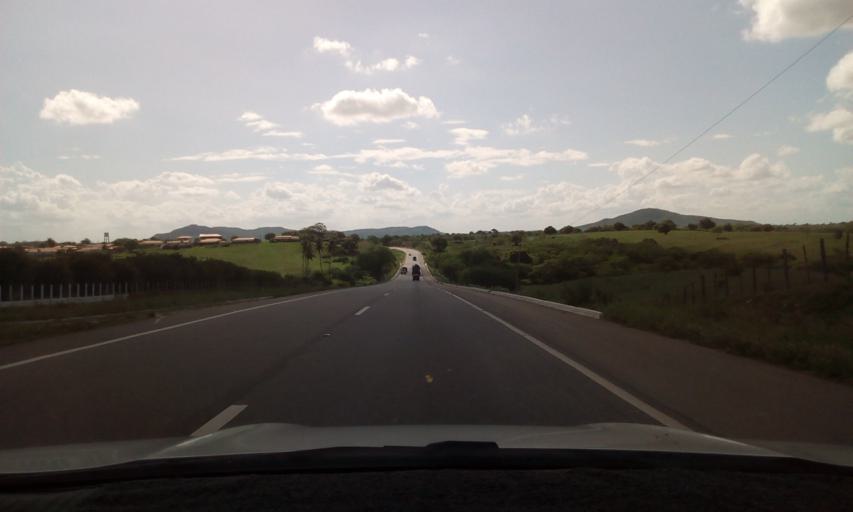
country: BR
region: Paraiba
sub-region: Gurinhem
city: Gurinhem
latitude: -7.1641
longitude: -35.3419
